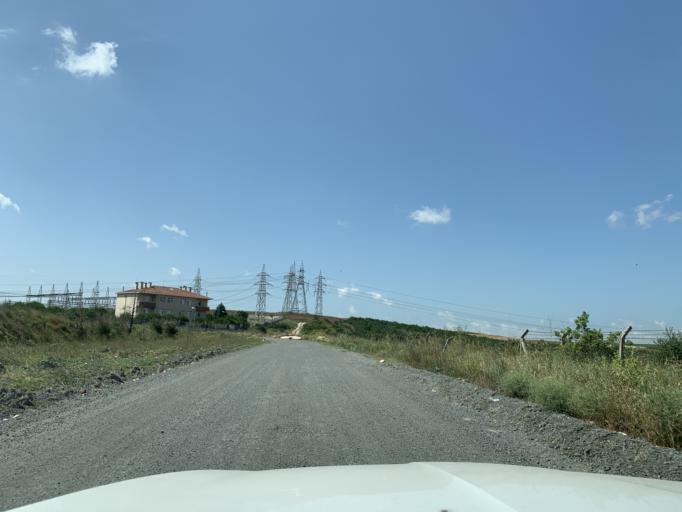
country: TR
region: Istanbul
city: Esenyurt
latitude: 41.0870
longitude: 28.6929
